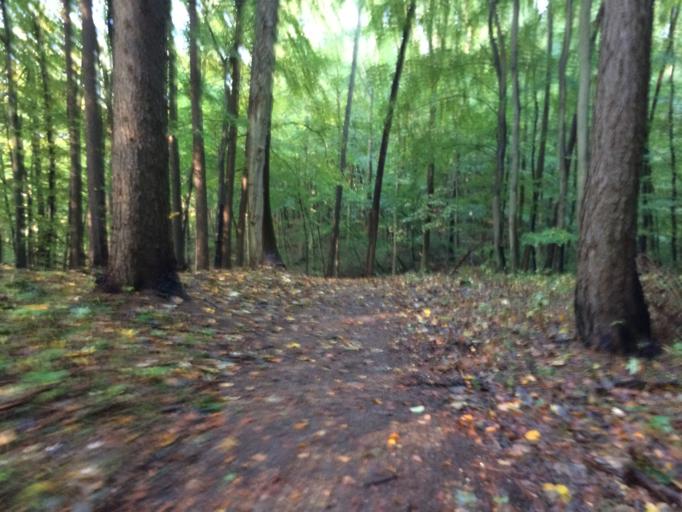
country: DK
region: Zealand
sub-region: Ringsted Kommune
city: Ringsted
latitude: 55.4879
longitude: 11.7963
